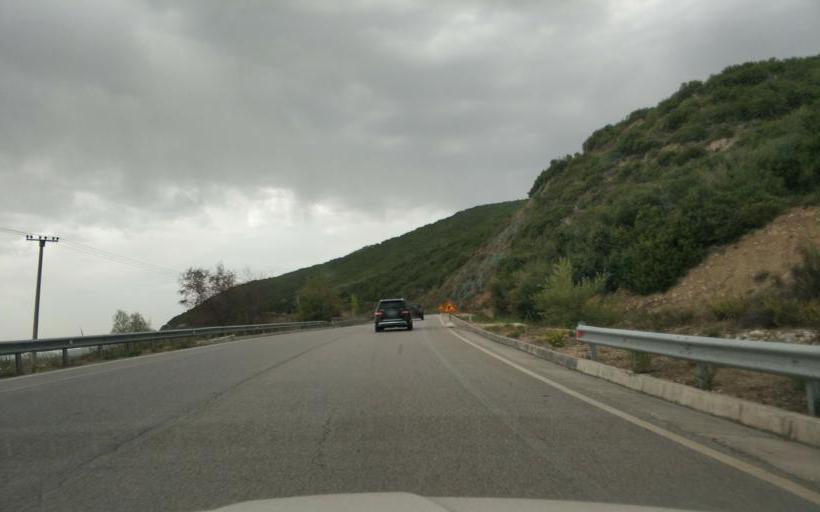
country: AL
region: Fier
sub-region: Rrethi i Mallakastres
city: Hekal
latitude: 40.5263
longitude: 19.7338
